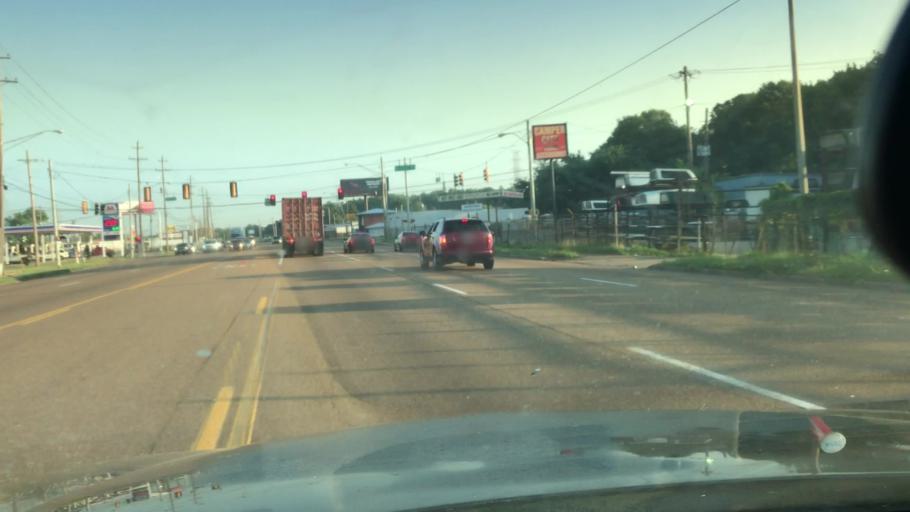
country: US
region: Mississippi
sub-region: De Soto County
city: Southaven
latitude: 35.0722
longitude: -89.9469
